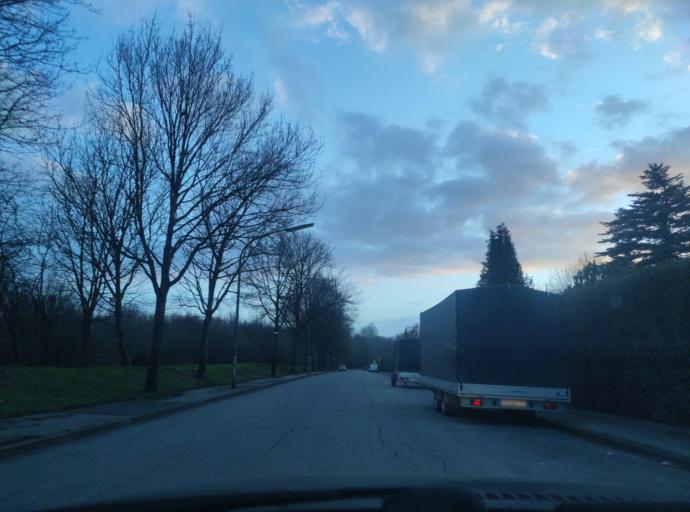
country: DE
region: North Rhine-Westphalia
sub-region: Regierungsbezirk Munster
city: Gelsenkirchen
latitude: 51.4871
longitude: 7.0884
